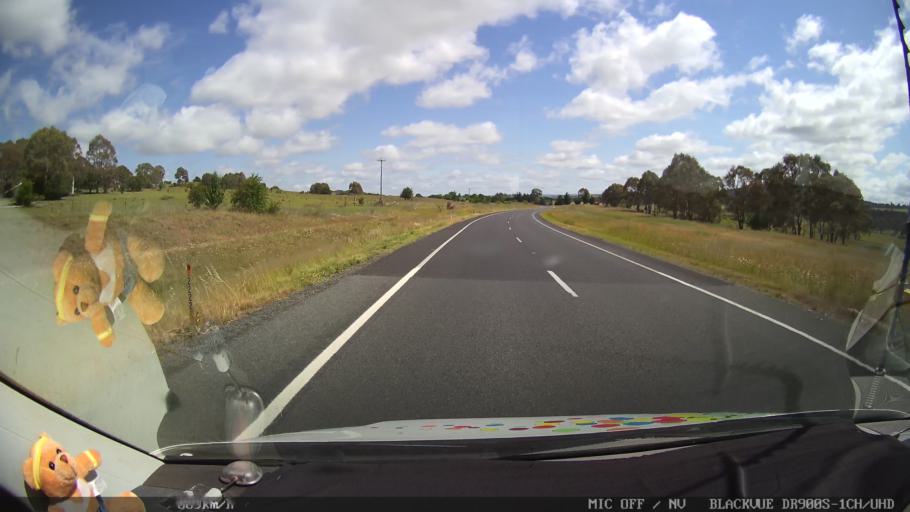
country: AU
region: New South Wales
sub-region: Glen Innes Severn
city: Glen Innes
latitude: -29.8884
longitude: 151.7332
